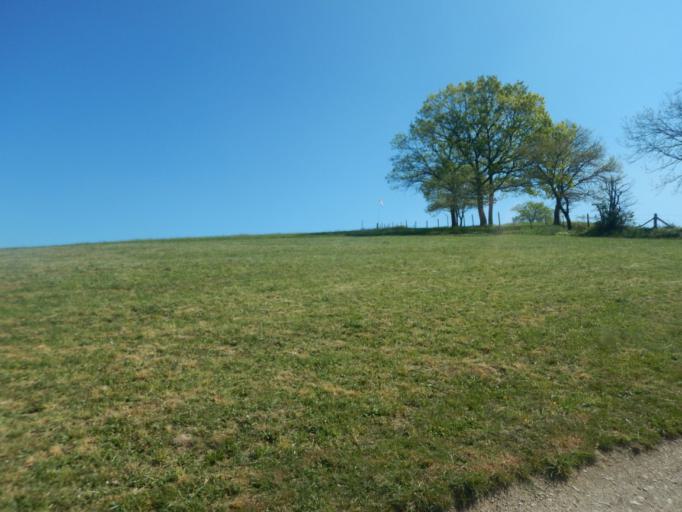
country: LU
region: Diekirch
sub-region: Canton de Diekirch
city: Bourscheid
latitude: 49.9158
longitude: 6.0916
